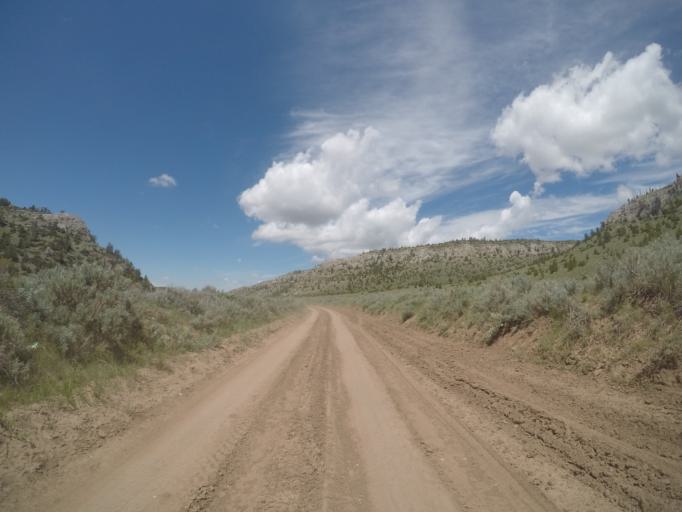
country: US
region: Wyoming
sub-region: Big Horn County
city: Lovell
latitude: 45.2286
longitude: -108.6022
